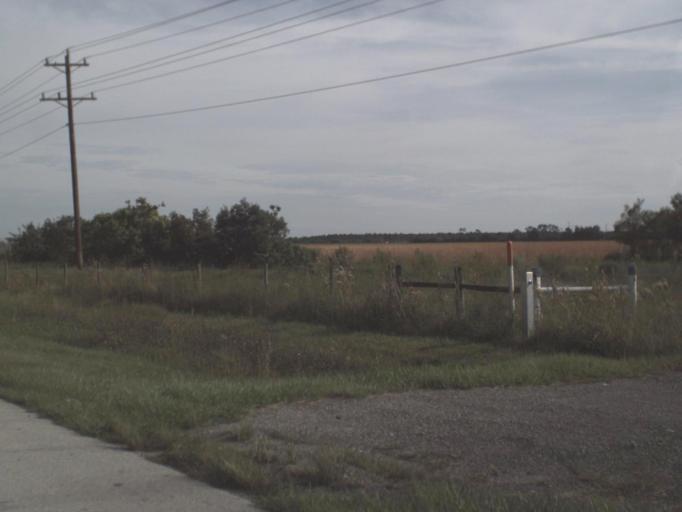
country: US
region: Florida
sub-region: Lee County
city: Fort Myers Shores
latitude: 26.7548
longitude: -81.7609
